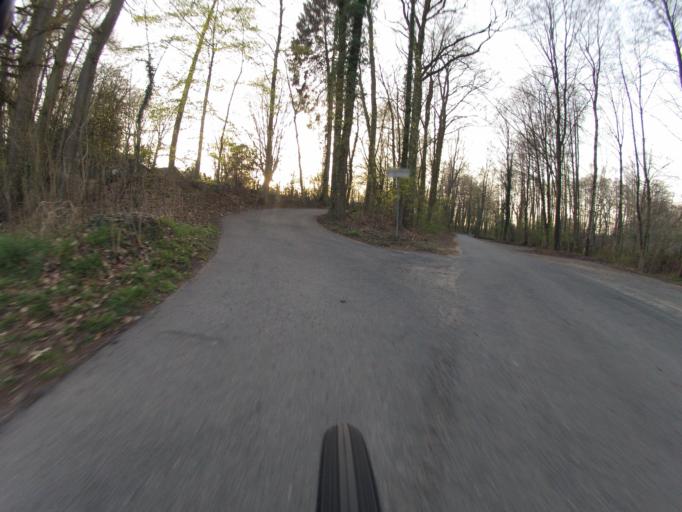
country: DE
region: North Rhine-Westphalia
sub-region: Regierungsbezirk Munster
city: Birgte
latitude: 52.2391
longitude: 7.6760
